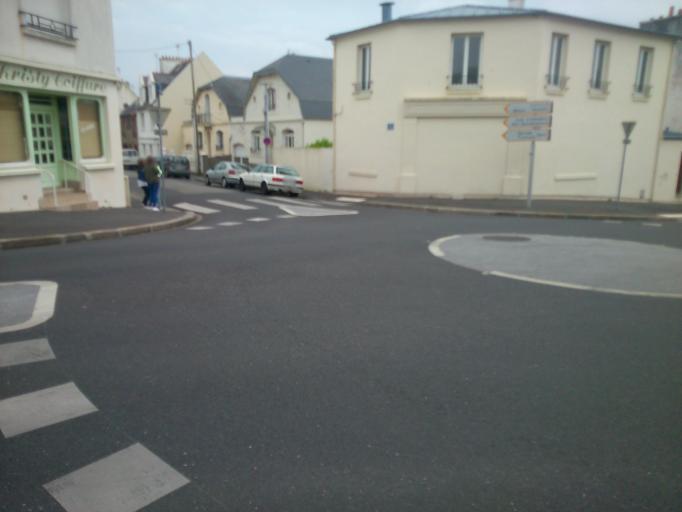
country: FR
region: Brittany
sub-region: Departement du Finistere
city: Brest
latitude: 48.3933
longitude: -4.4746
